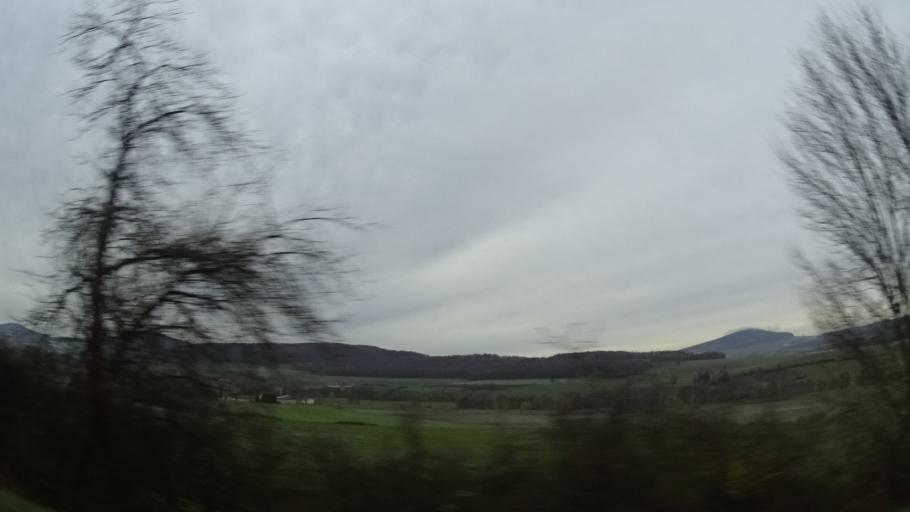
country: DE
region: Thuringia
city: Buttlar
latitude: 50.7404
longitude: 9.9330
